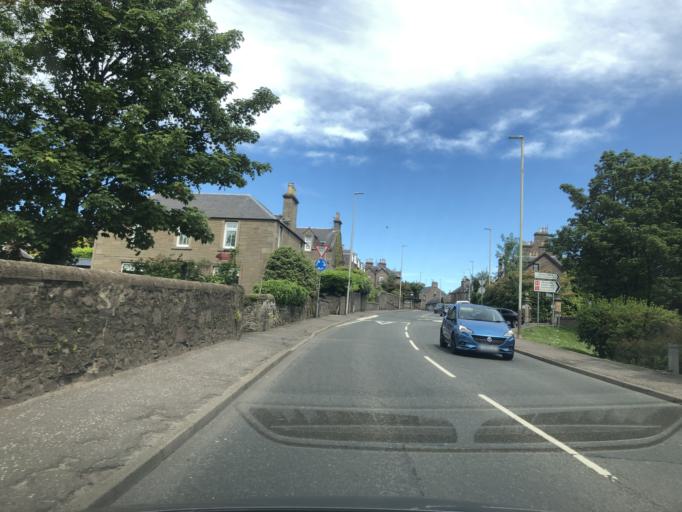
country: GB
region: Scotland
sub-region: Angus
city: Forfar
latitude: 56.6491
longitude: -2.8893
